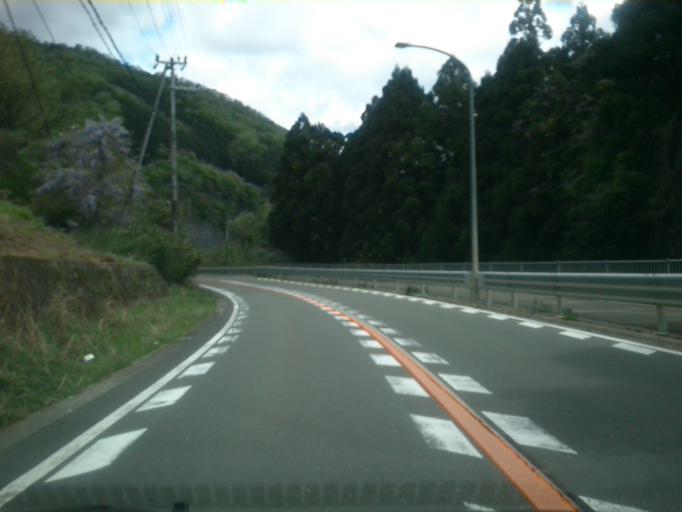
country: JP
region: Kyoto
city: Ayabe
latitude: 35.2006
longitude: 135.4225
